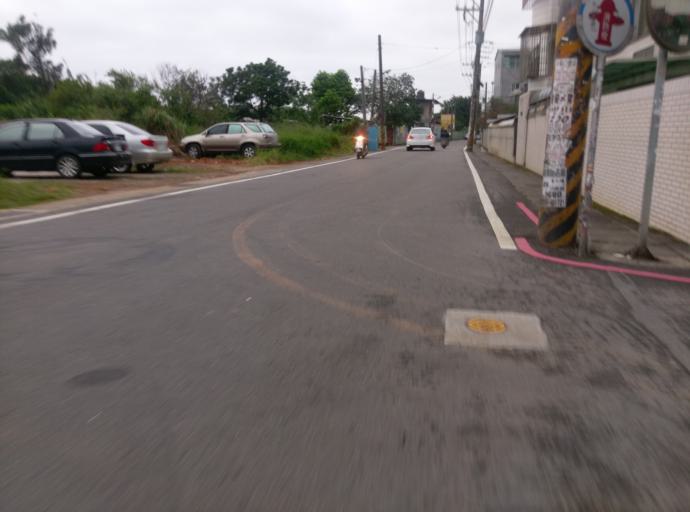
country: TW
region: Taiwan
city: Daxi
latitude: 24.9141
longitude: 121.2384
